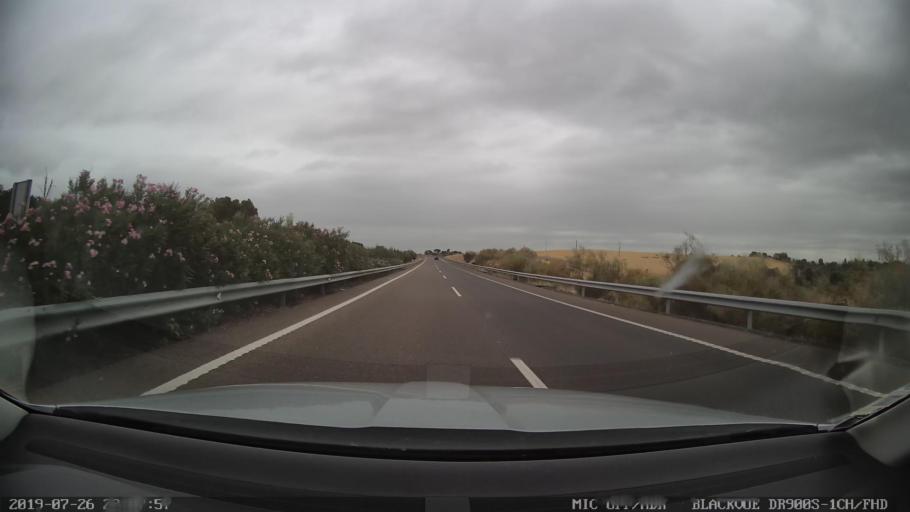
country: ES
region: Extremadura
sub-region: Provincia de Badajoz
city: San Pedro de Merida
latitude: 38.9495
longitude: -6.1706
